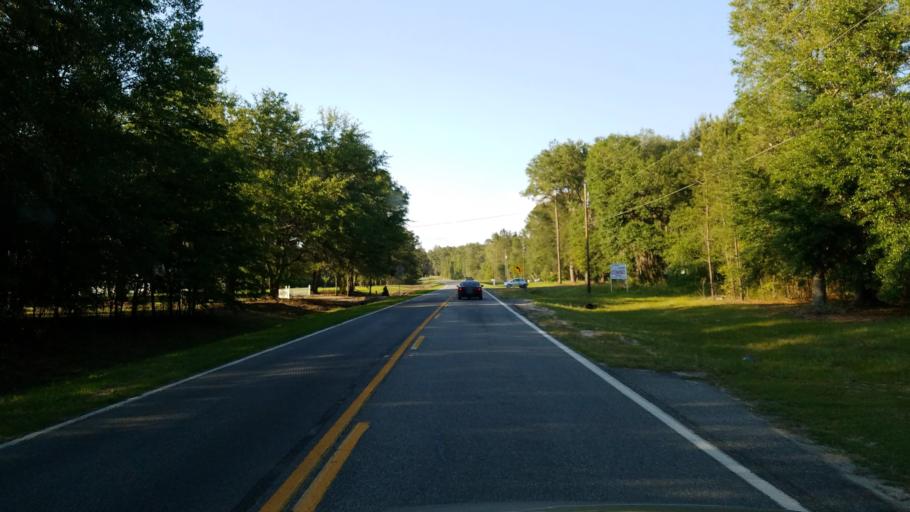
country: US
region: Georgia
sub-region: Lanier County
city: Lakeland
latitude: 31.0016
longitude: -83.0669
